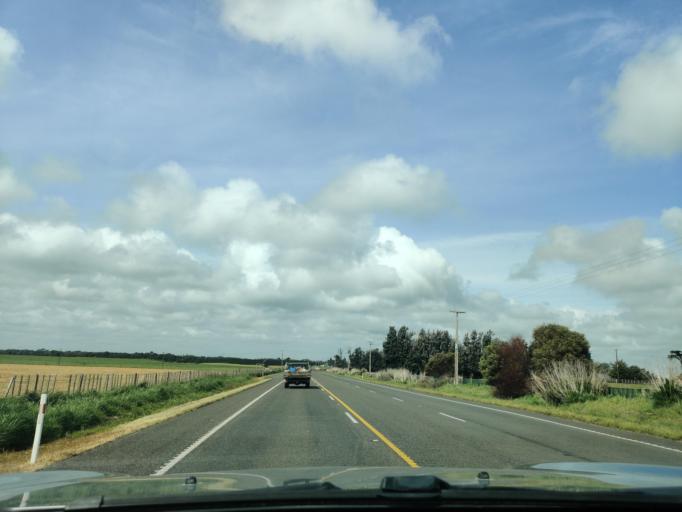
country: NZ
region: Taranaki
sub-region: South Taranaki District
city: Patea
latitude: -39.7669
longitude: 174.6082
